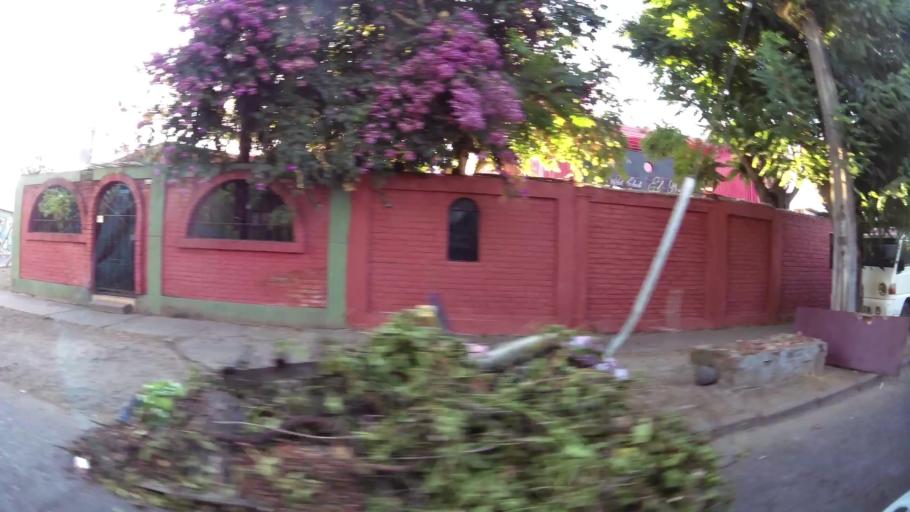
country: CL
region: Maule
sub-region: Provincia de Curico
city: Curico
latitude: -34.9971
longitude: -71.2369
